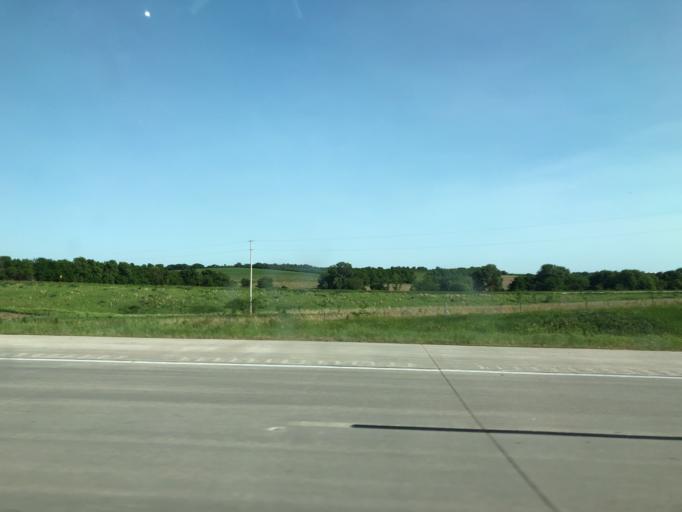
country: US
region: Nebraska
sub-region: Saunders County
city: Ashland
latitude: 40.9939
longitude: -96.3493
